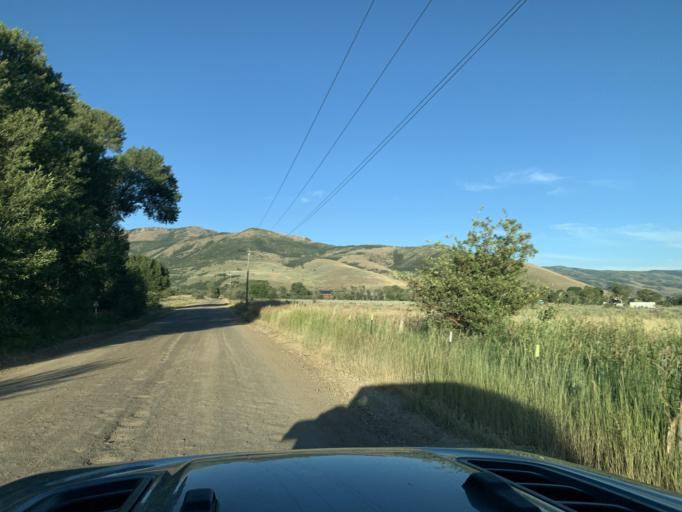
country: US
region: Utah
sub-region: Weber County
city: Wolf Creek
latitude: 41.2931
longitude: -111.7679
